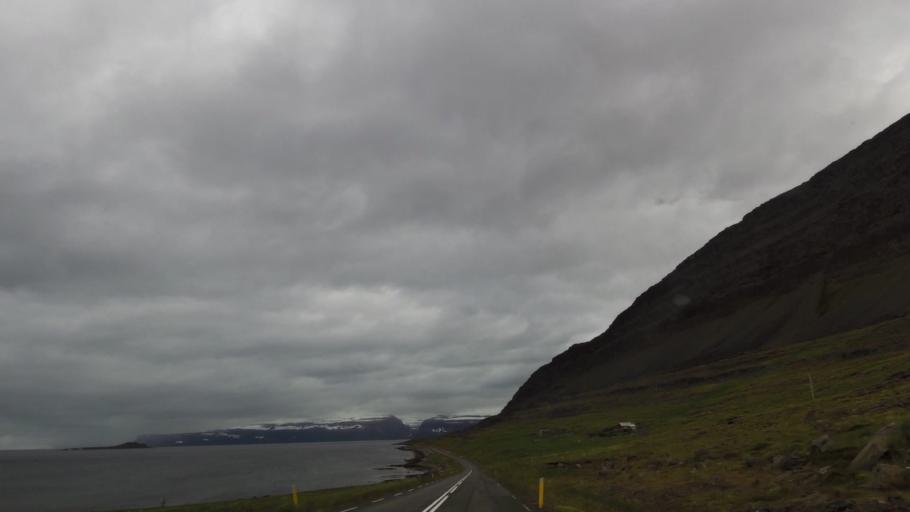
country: IS
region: Westfjords
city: Isafjoerdur
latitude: 66.0071
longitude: -22.7838
